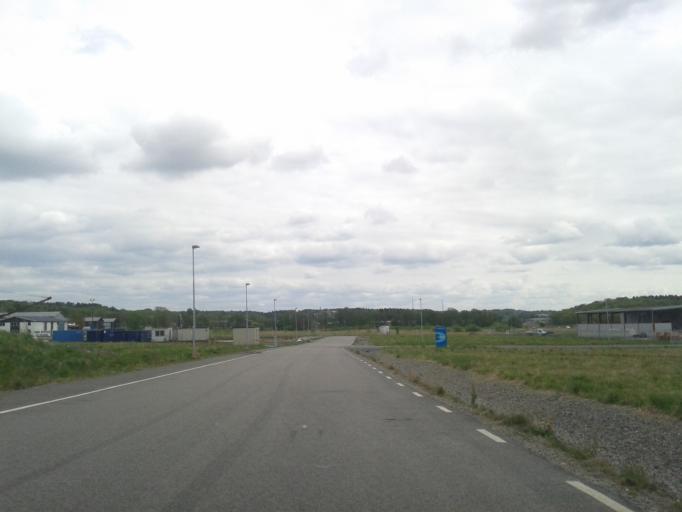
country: SE
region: Vaestra Goetaland
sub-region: Kungalvs Kommun
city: Kungalv
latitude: 57.8982
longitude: 11.9291
